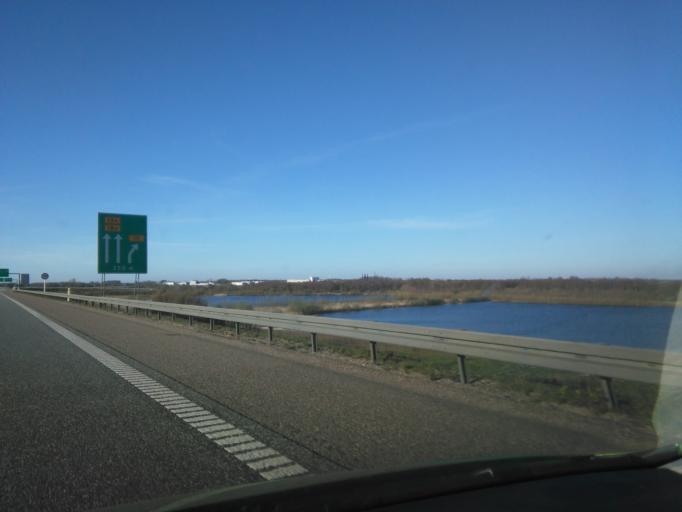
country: DK
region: Central Jutland
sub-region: Herning Kommune
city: Lind
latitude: 56.1169
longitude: 9.0114
